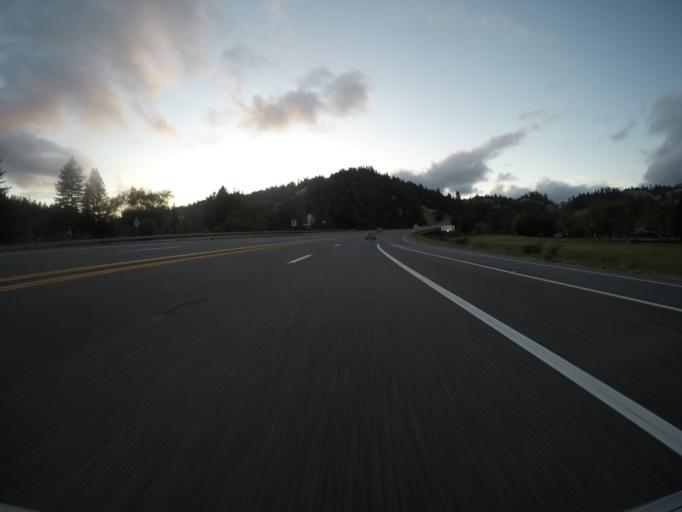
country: US
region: California
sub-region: Humboldt County
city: Redway
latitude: 40.0663
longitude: -123.7874
